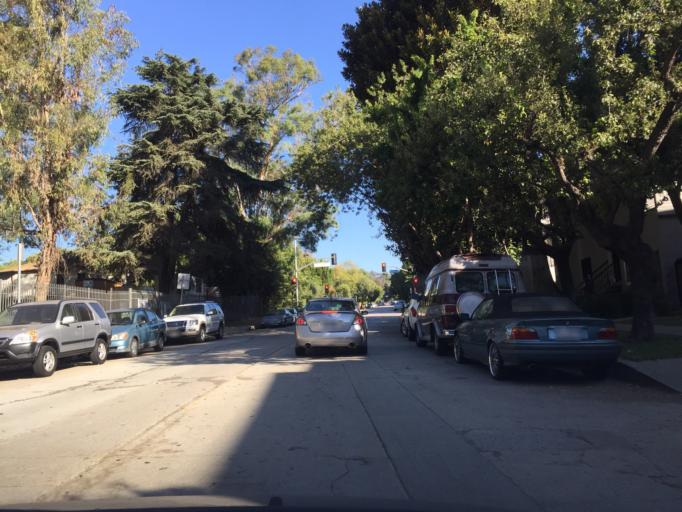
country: US
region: California
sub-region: Los Angeles County
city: Westwood, Los Angeles
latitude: 34.0661
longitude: -118.4546
